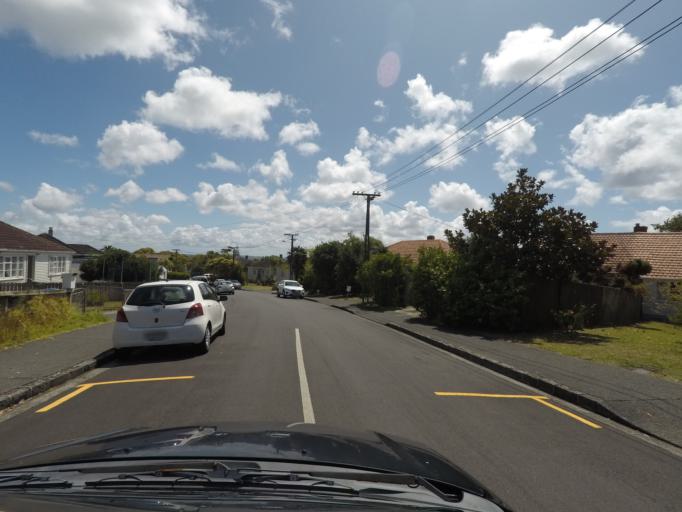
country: NZ
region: Auckland
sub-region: Auckland
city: Auckland
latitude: -36.8599
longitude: 174.7218
